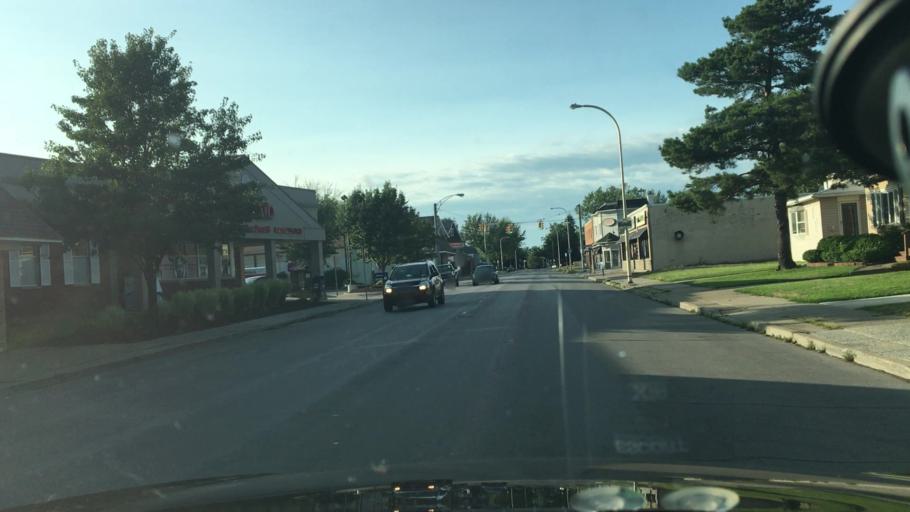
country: US
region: New York
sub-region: Erie County
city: West Seneca
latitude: 42.8411
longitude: -78.8085
